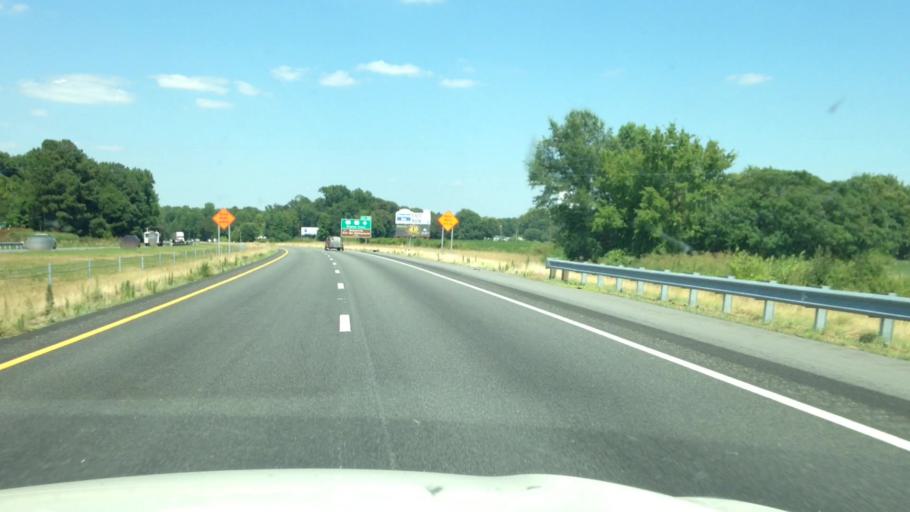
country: US
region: North Carolina
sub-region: Johnston County
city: Four Oaks
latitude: 35.4444
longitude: -78.4056
